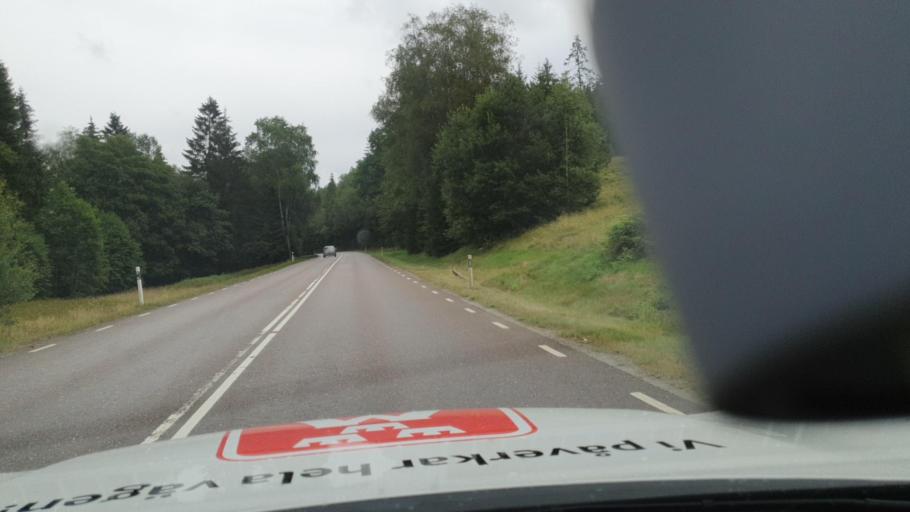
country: SE
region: Vaestra Goetaland
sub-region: Harryda Kommun
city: Landvetter
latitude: 57.6054
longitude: 12.2325
